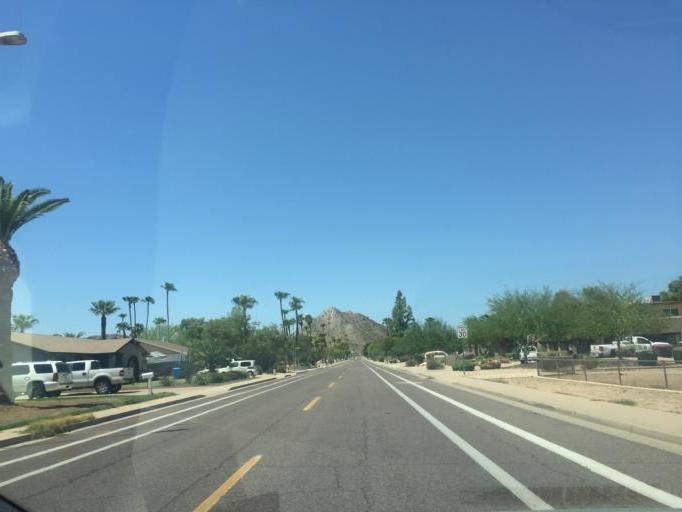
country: US
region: Arizona
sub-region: Maricopa County
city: Paradise Valley
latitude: 33.5896
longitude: -112.0225
